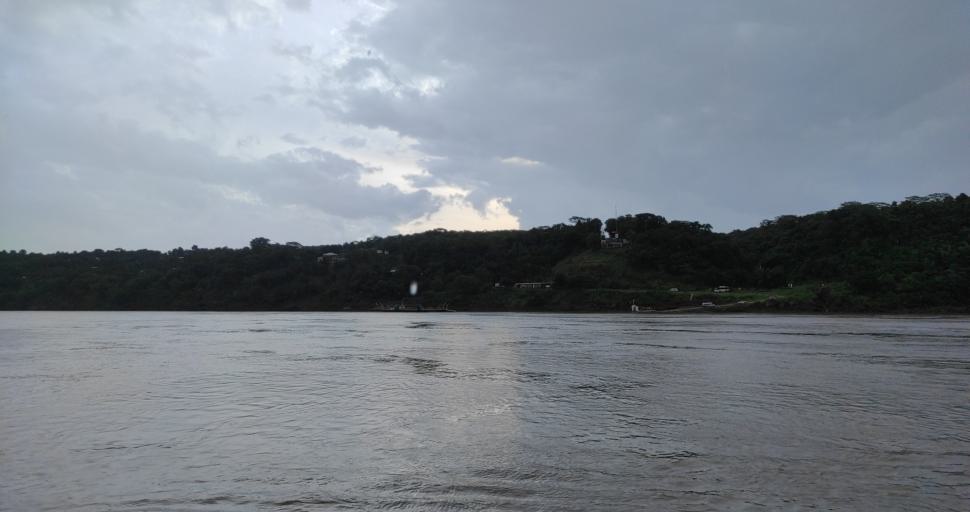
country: AR
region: Misiones
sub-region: Departamento de Iguazu
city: Puerto Iguazu
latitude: -25.5918
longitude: -54.5919
